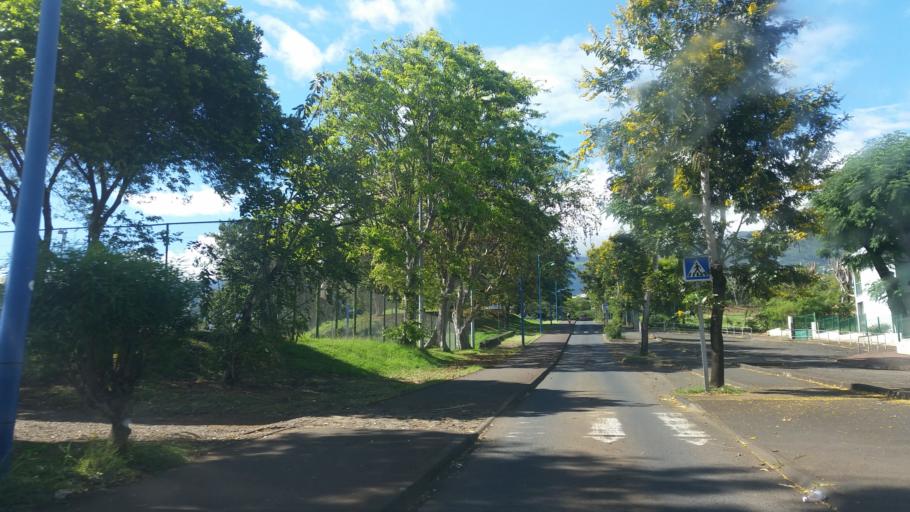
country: RE
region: Reunion
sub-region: Reunion
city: Saint-Denis
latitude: -20.8970
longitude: 55.4863
